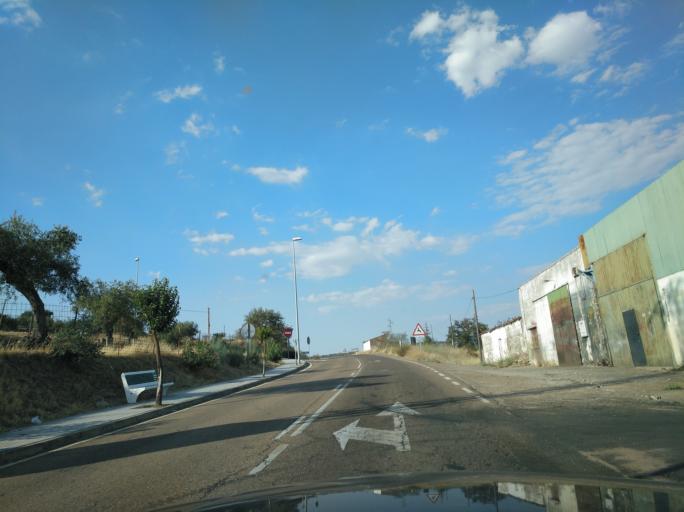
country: ES
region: Extremadura
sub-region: Provincia de Badajoz
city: Alconchel
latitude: 38.5192
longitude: -7.0659
